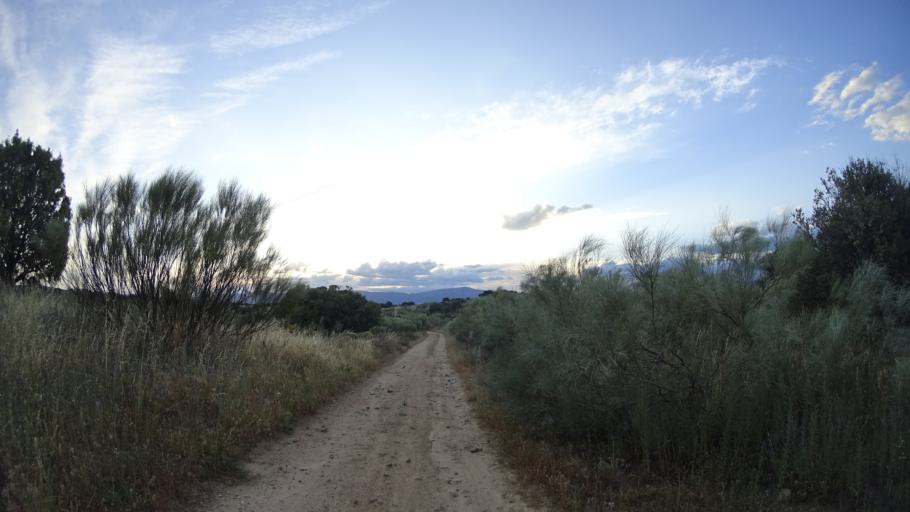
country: ES
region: Madrid
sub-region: Provincia de Madrid
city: Colmenarejo
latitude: 40.5315
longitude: -3.9987
